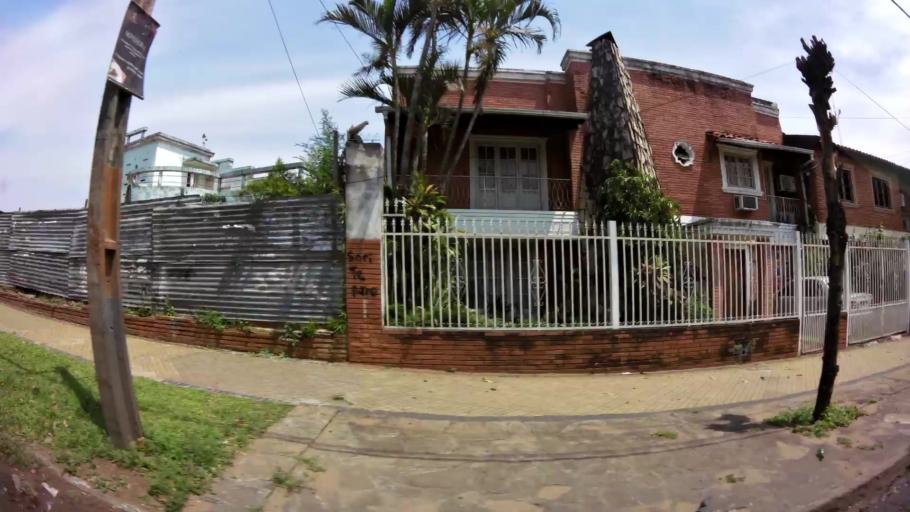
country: PY
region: Central
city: Lambare
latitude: -25.3124
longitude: -57.5975
